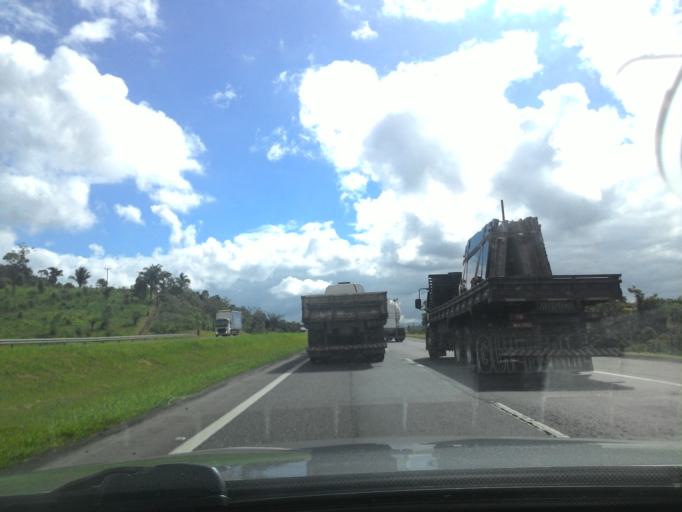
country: BR
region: Sao Paulo
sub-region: Cajati
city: Cajati
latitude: -24.9250
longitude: -48.2648
